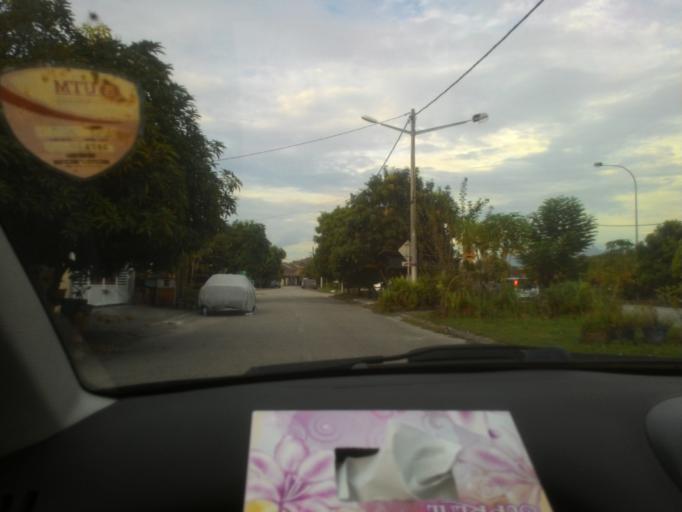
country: MY
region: Perak
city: Ipoh
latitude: 4.6765
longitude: 101.0823
